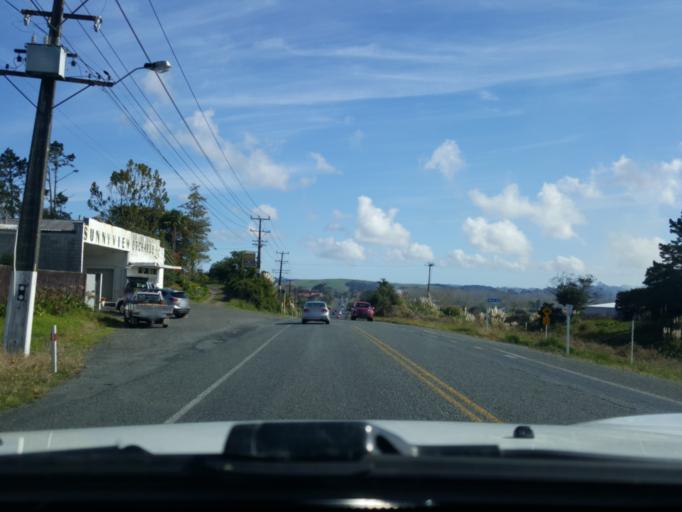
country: NZ
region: Auckland
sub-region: Auckland
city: Muriwai Beach
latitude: -36.7667
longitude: 174.5171
